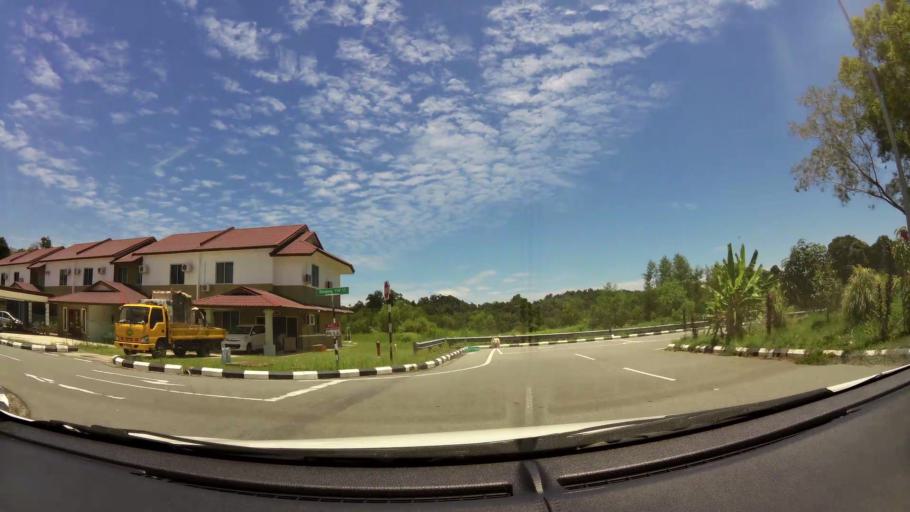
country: BN
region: Brunei and Muara
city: Bandar Seri Begawan
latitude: 5.0085
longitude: 115.0045
